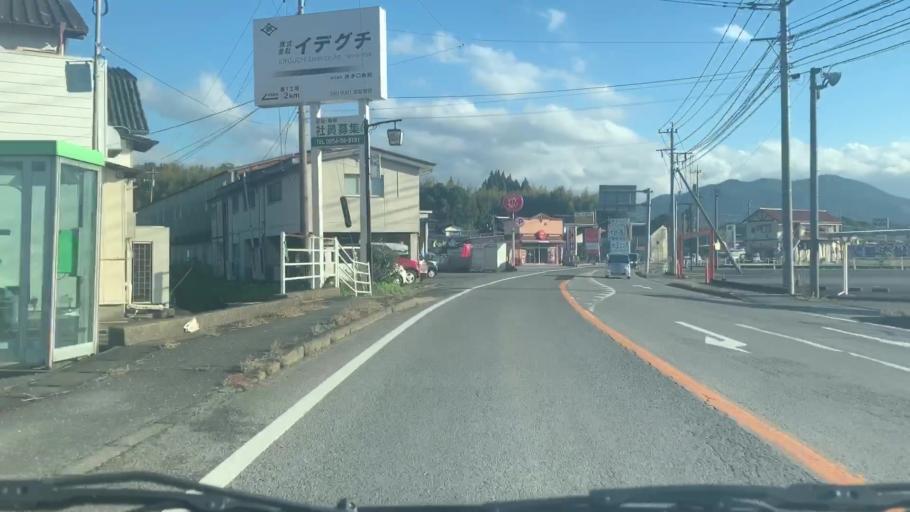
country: JP
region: Saga Prefecture
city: Takeocho-takeo
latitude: 33.2198
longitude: 130.0532
